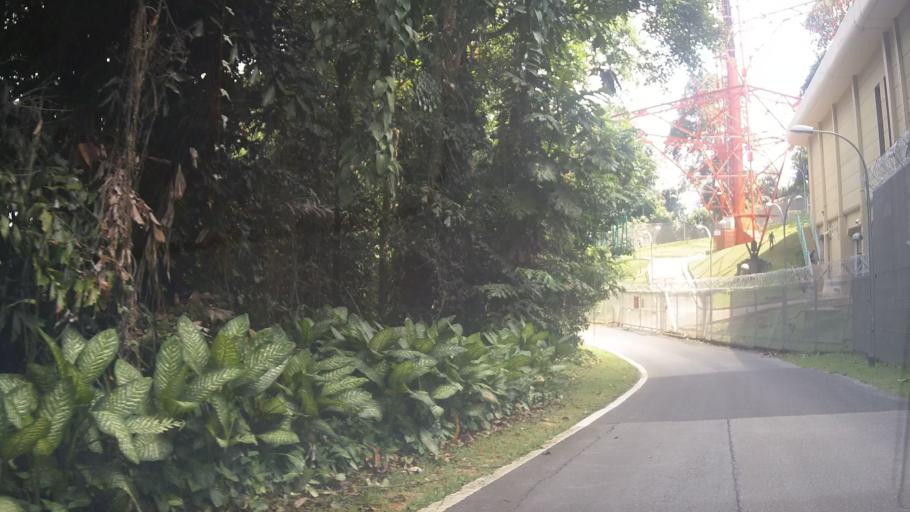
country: SG
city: Singapore
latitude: 1.3523
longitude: 103.7663
